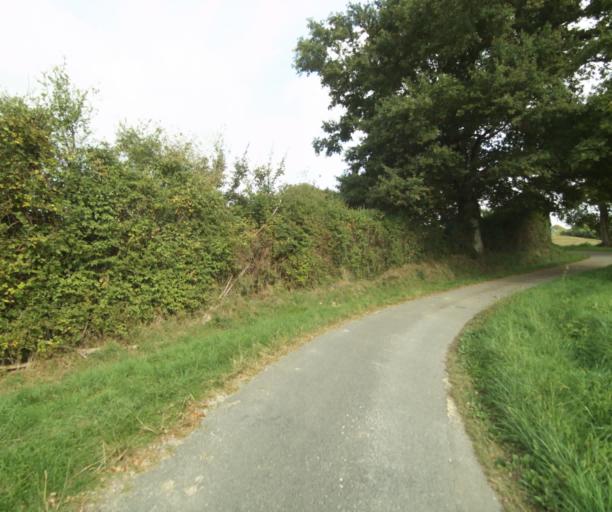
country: FR
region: Midi-Pyrenees
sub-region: Departement du Gers
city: Gondrin
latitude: 43.8360
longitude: 0.1893
